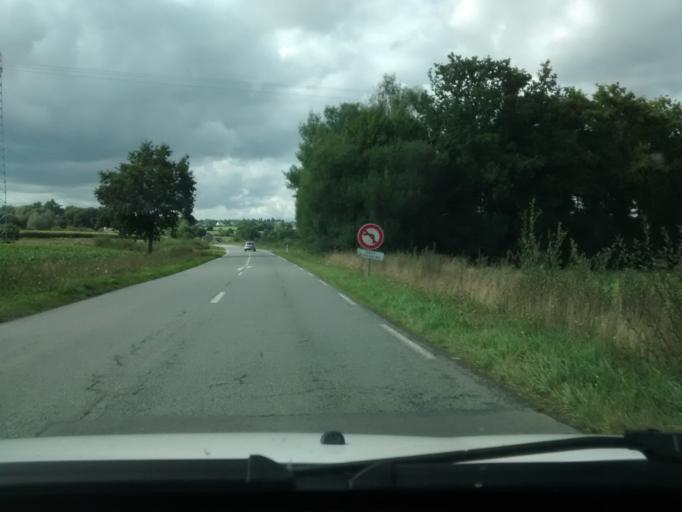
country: FR
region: Brittany
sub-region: Departement d'Ille-et-Vilaine
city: Miniac-Morvan
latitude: 48.5083
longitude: -1.8820
